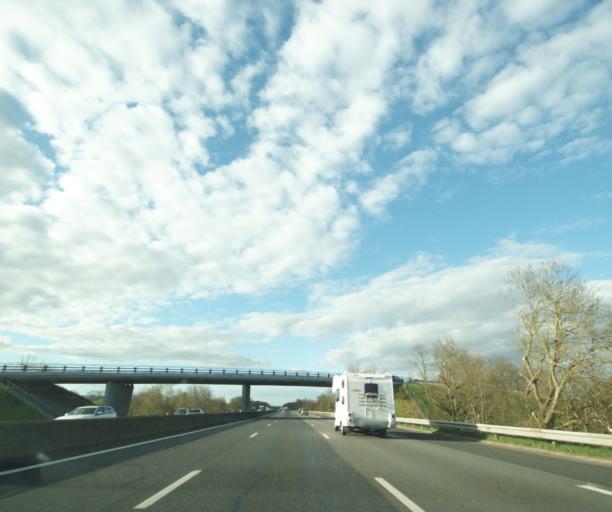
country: FR
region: Rhone-Alpes
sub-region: Departement de l'Ain
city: Thoissey
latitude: 46.1582
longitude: 4.7707
